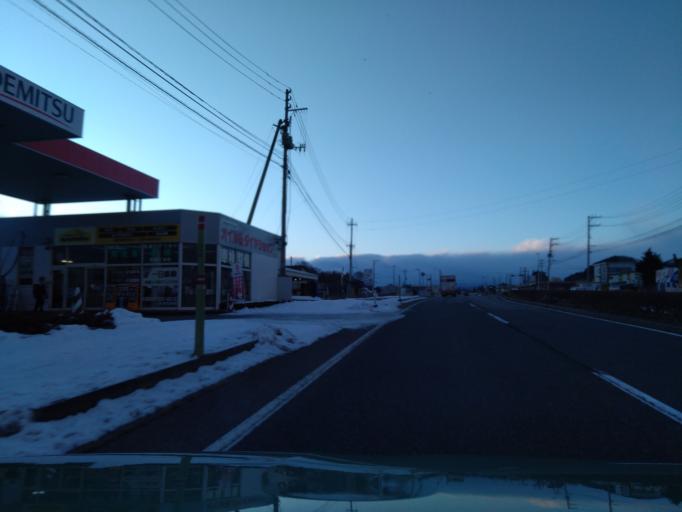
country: JP
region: Iwate
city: Shizukuishi
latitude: 39.6996
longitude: 141.0552
